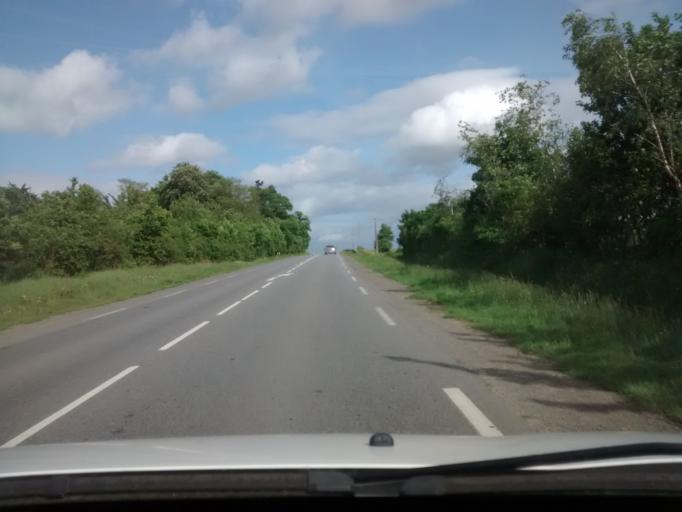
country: FR
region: Brittany
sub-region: Departement d'Ille-et-Vilaine
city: Vern-sur-Seiche
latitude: 48.0477
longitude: -1.5817
